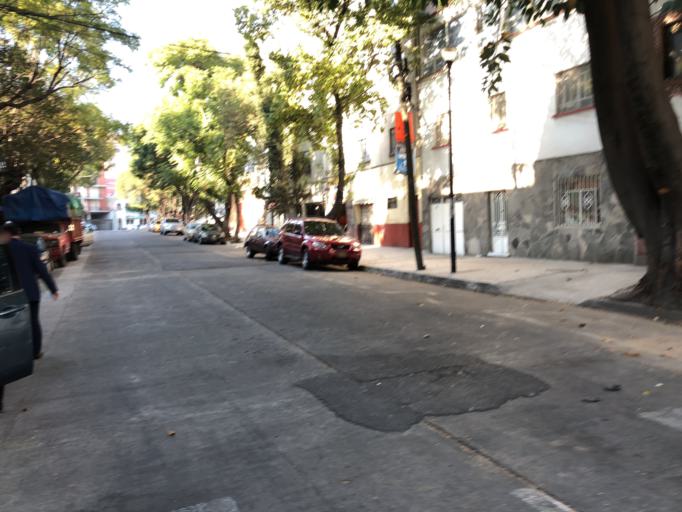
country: MX
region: Mexico City
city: Cuauhtemoc
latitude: 19.4327
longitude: -99.1698
